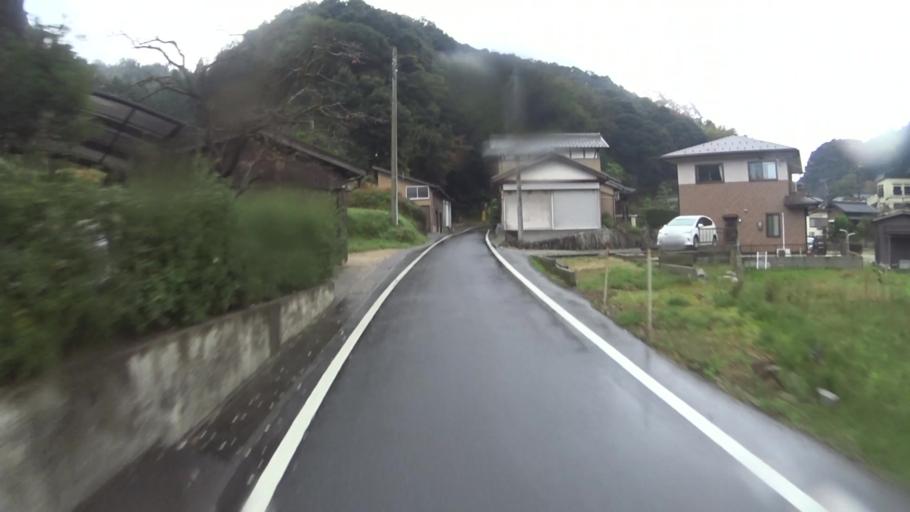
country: JP
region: Kyoto
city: Miyazu
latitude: 35.5338
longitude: 135.2134
